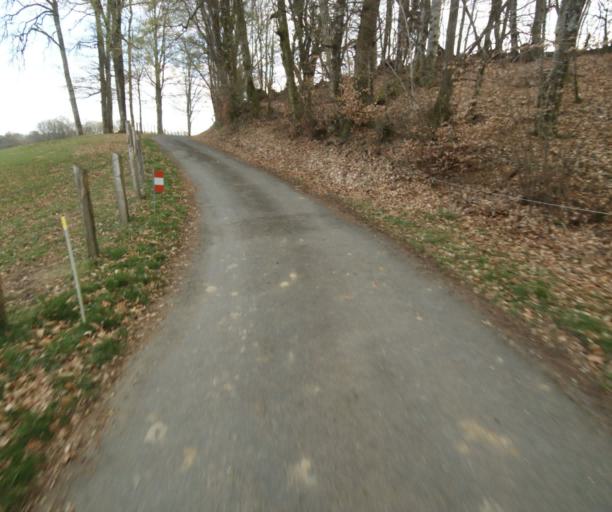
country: FR
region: Limousin
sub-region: Departement de la Correze
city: Saint-Clement
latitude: 45.3600
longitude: 1.6443
